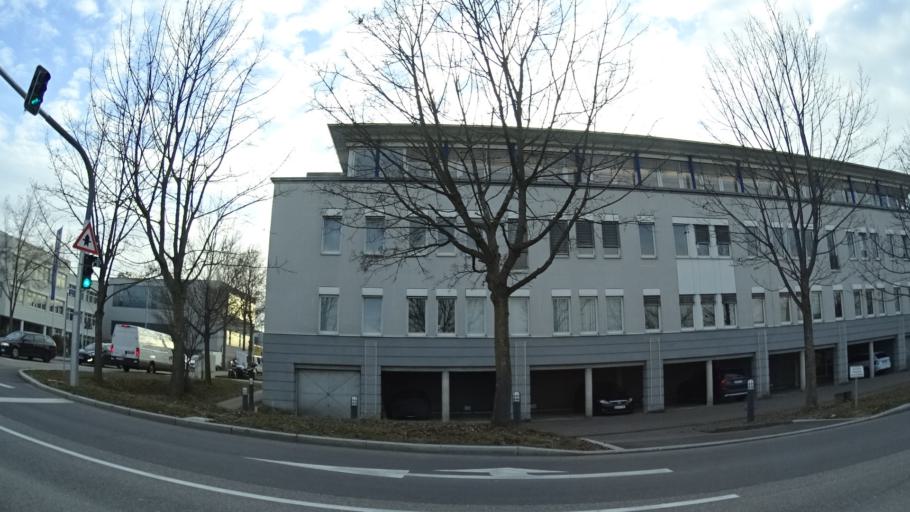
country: DE
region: Baden-Wuerttemberg
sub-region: Regierungsbezirk Stuttgart
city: Ditzingen
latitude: 48.8207
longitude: 9.0639
